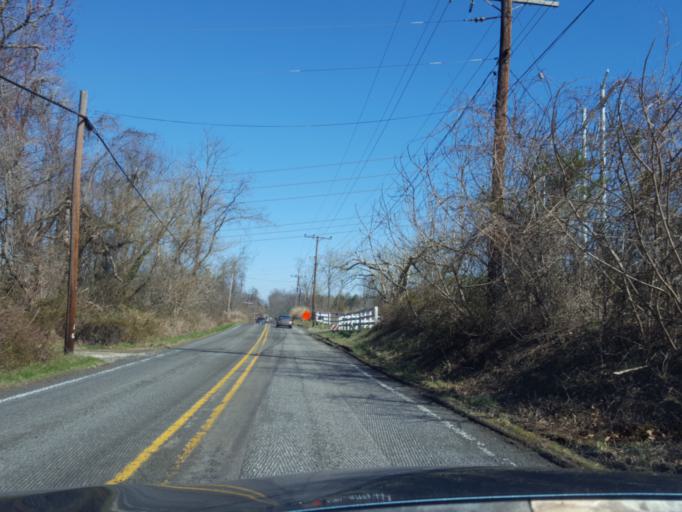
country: US
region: Maryland
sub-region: Anne Arundel County
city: Deale
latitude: 38.7794
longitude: -76.5902
